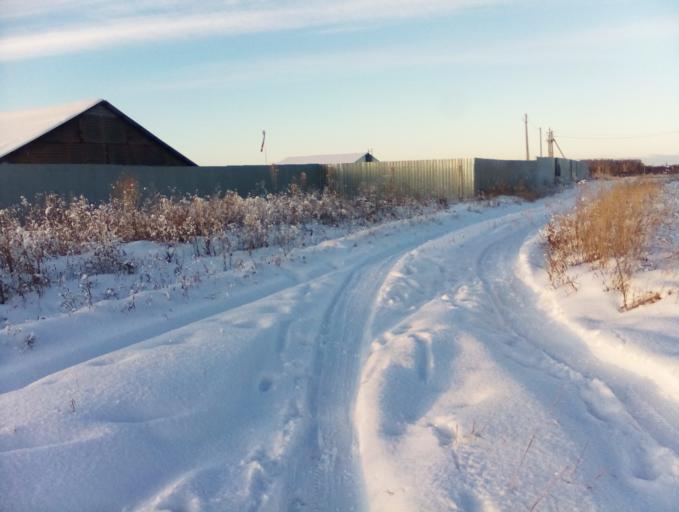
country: RU
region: Chelyabinsk
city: Poletayevo
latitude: 54.9841
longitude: 60.9470
